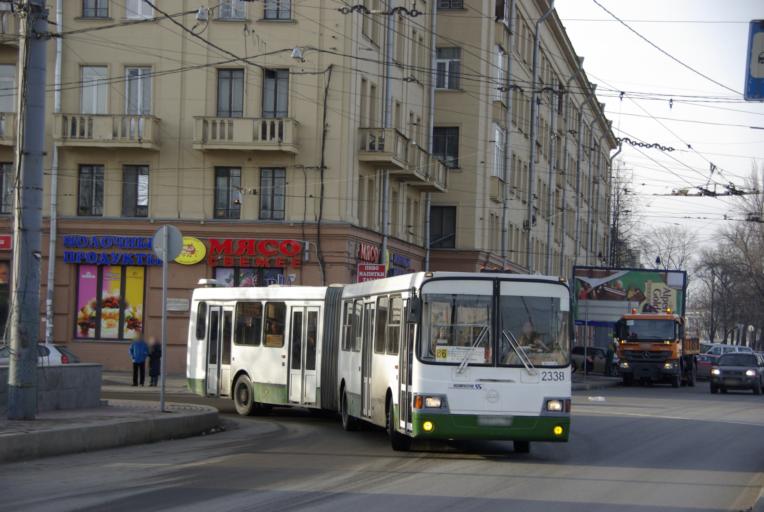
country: RU
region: Leningrad
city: Sampsonievskiy
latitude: 59.9711
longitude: 30.3483
